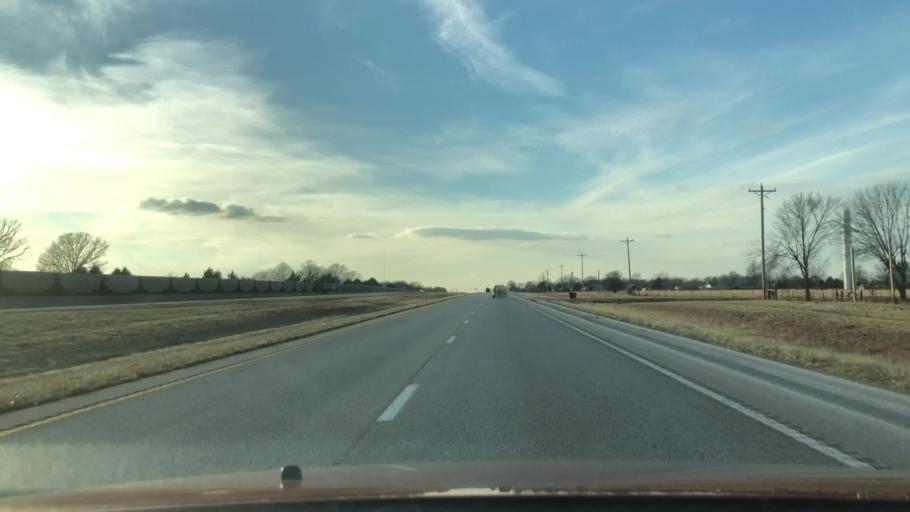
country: US
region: Missouri
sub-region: Webster County
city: Seymour
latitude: 37.1712
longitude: -92.8397
